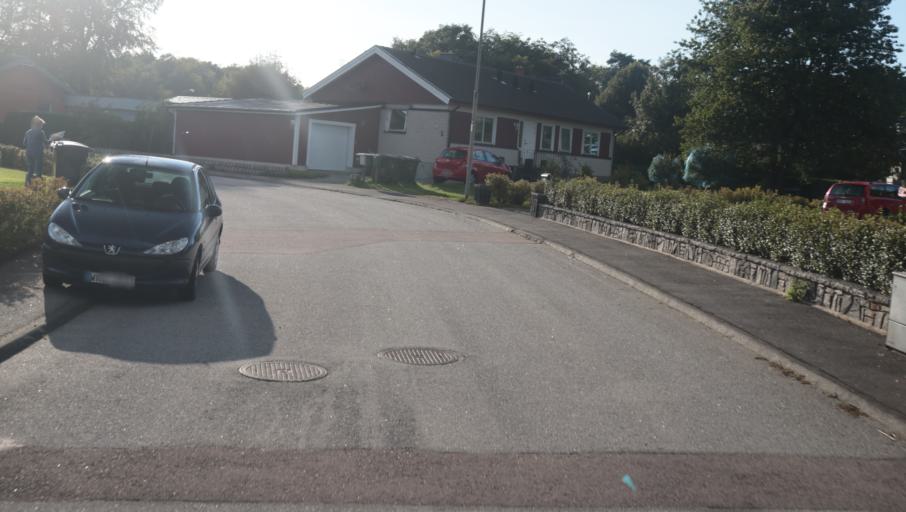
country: SE
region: Blekinge
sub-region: Karlshamns Kommun
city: Karlshamn
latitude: 56.1628
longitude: 14.8860
